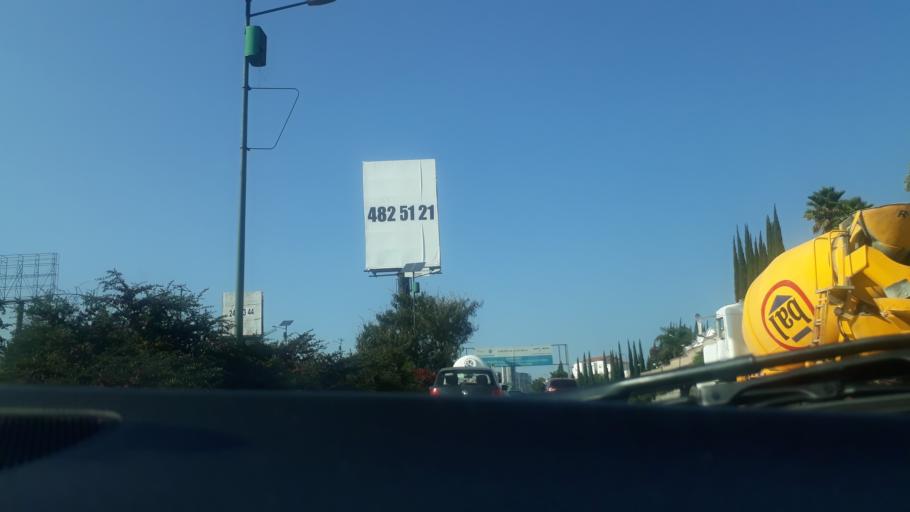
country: MX
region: Puebla
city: Tlazcalancingo
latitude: 19.0014
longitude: -98.2605
